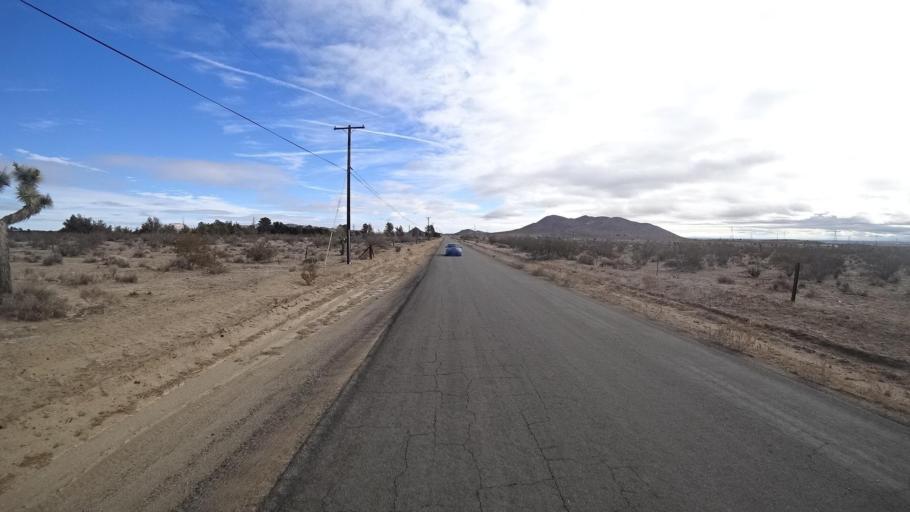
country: US
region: California
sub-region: Kern County
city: Rosamond
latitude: 34.8926
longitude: -118.3137
